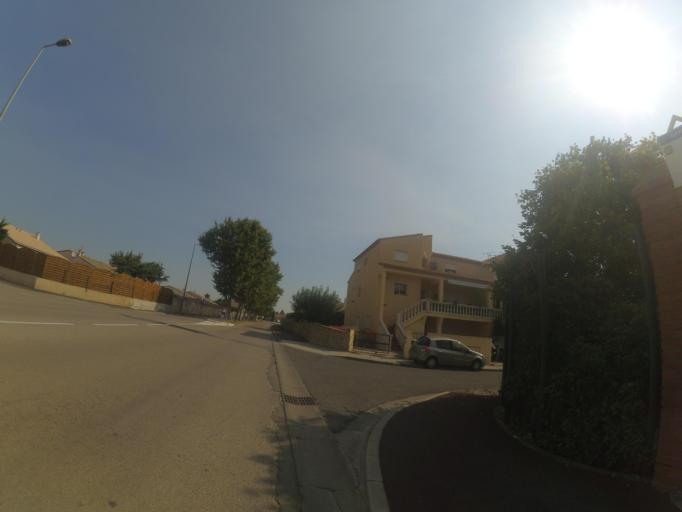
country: FR
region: Languedoc-Roussillon
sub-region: Departement des Pyrenees-Orientales
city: Toulouges
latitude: 42.6663
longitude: 2.8376
